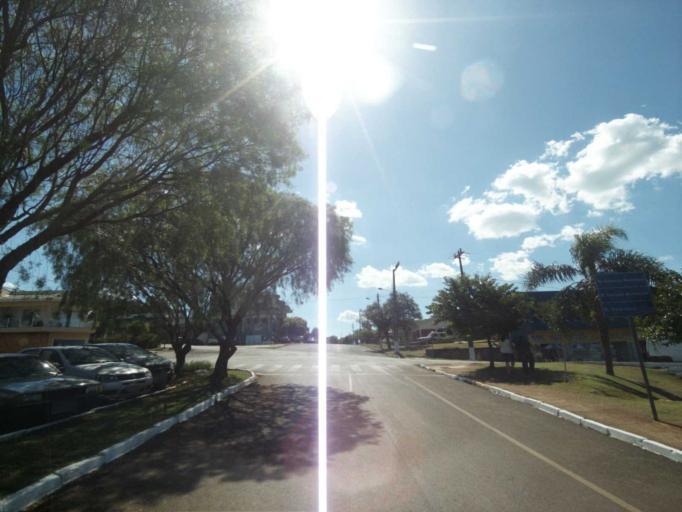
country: BR
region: Parana
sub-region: Laranjeiras Do Sul
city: Laranjeiras do Sul
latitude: -25.3817
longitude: -52.2043
